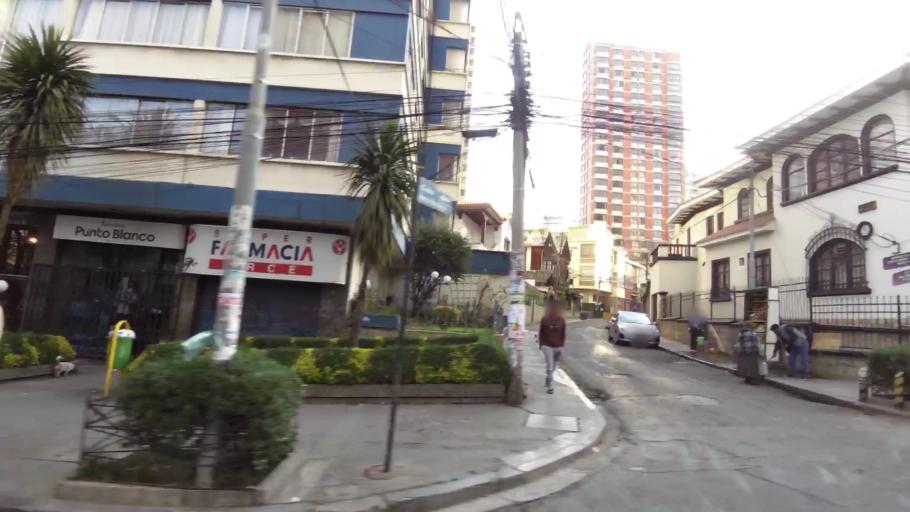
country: BO
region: La Paz
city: La Paz
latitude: -16.5100
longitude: -68.1235
